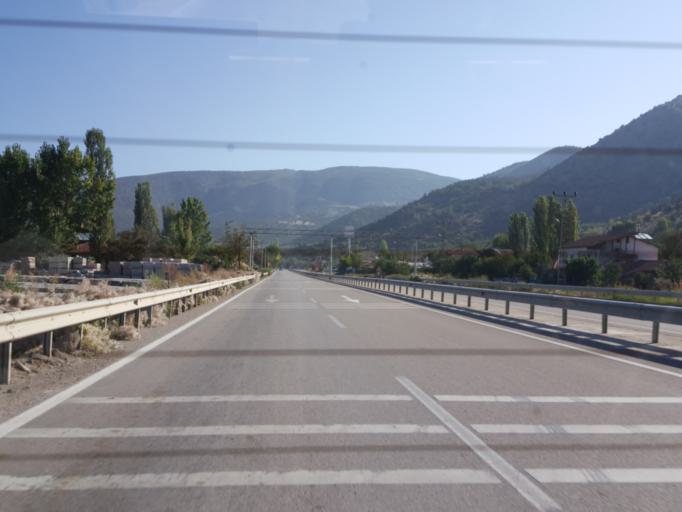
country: TR
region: Tokat
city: Turhal
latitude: 40.4135
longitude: 36.1052
